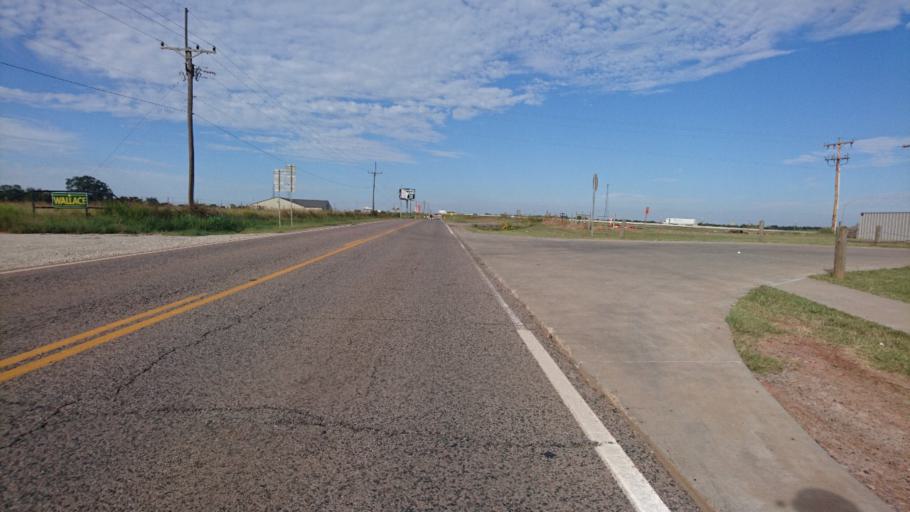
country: US
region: Oklahoma
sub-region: Oklahoma County
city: Luther
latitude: 35.6811
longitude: -97.0406
